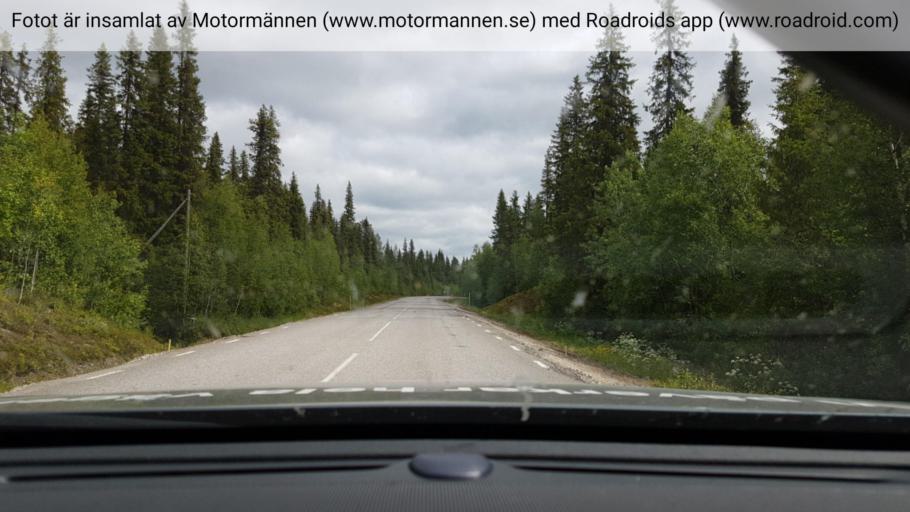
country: SE
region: Vaesterbotten
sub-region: Storumans Kommun
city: Fristad
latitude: 65.8077
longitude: 16.9287
